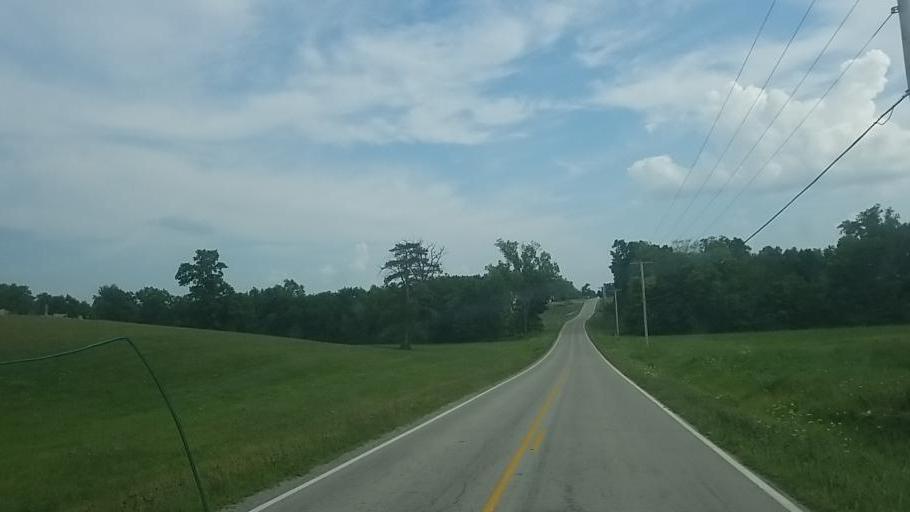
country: US
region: Ohio
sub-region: Wyandot County
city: Upper Sandusky
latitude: 40.7949
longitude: -83.2784
